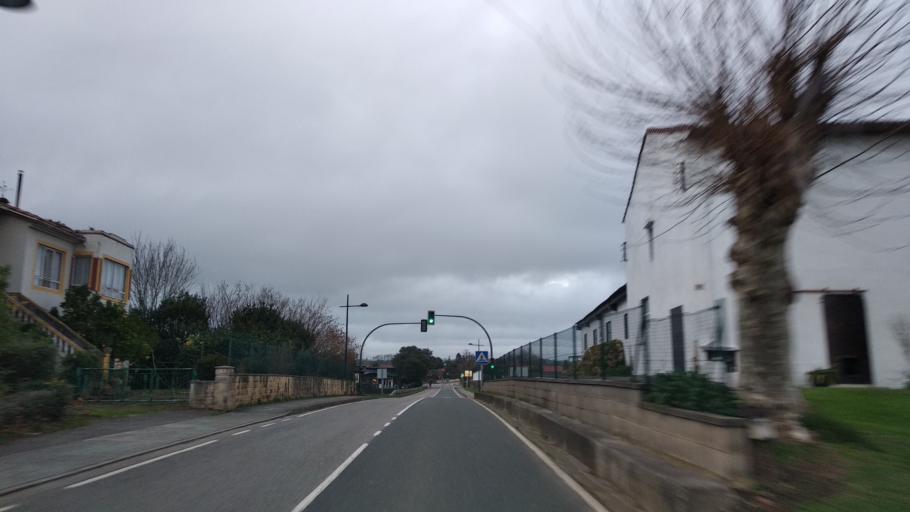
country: ES
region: Cantabria
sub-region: Provincia de Cantabria
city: Entrambasaguas
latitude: 43.4388
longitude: -3.7150
